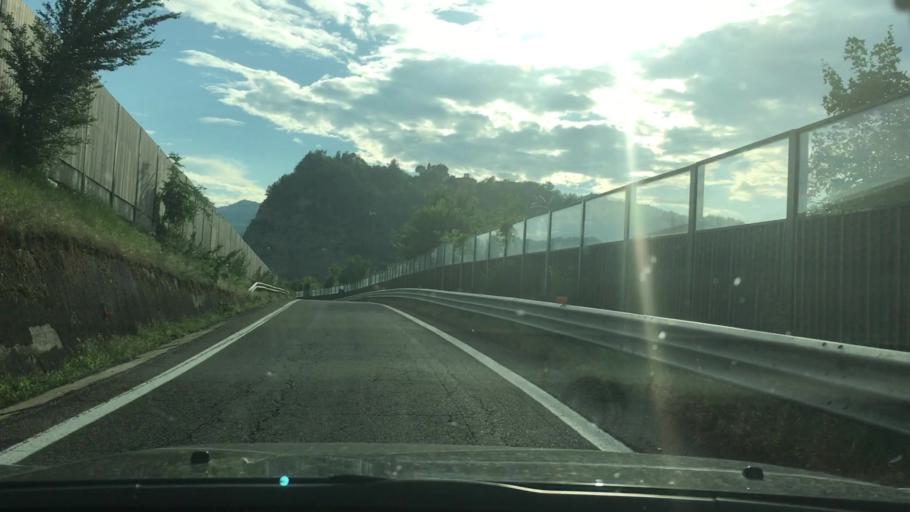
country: IT
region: Emilia-Romagna
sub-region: Provincia di Bologna
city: Sasso Marconi
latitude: 44.3898
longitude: 11.2514
